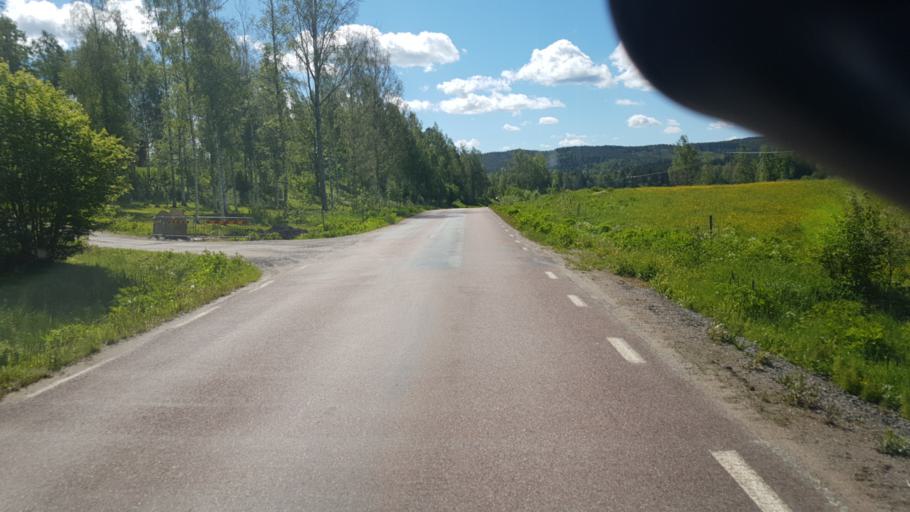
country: SE
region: Vaermland
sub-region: Arvika Kommun
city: Arvika
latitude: 59.5298
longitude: 12.8246
